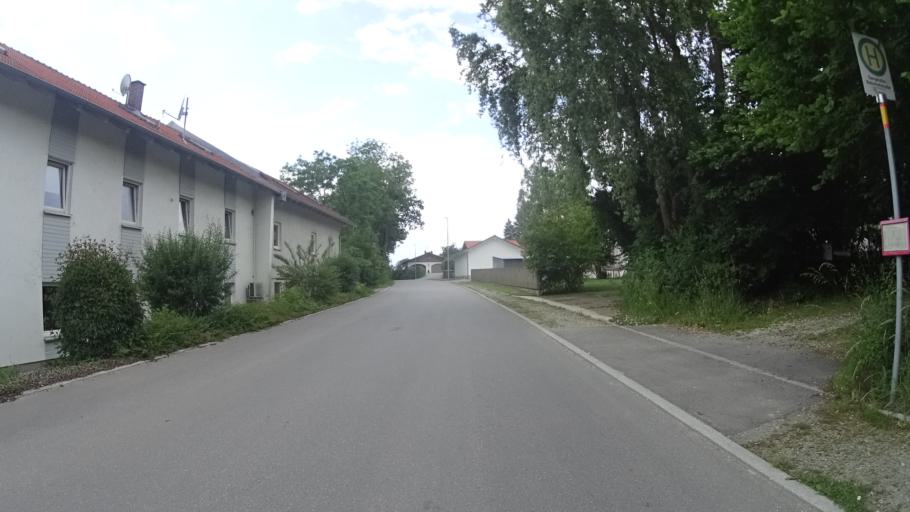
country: DE
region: Bavaria
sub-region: Lower Bavaria
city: Gangkofen
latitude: 48.4404
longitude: 12.5525
